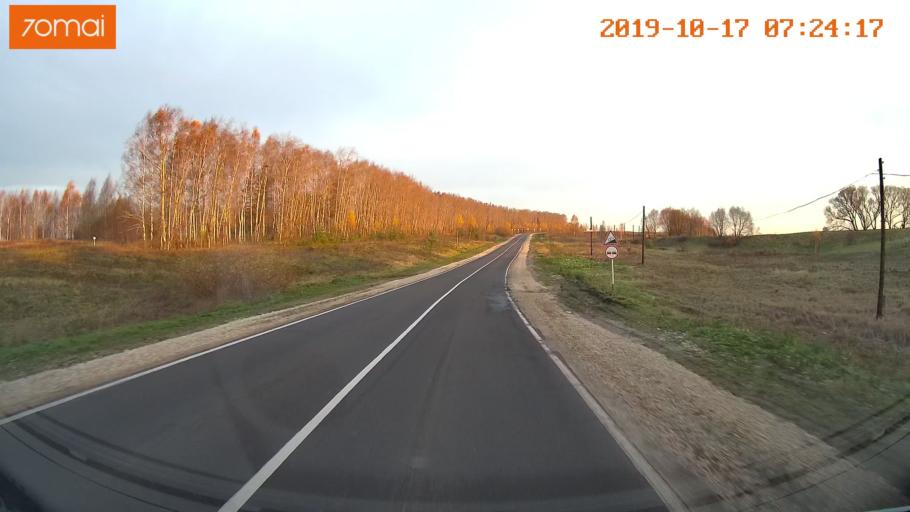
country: RU
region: Ivanovo
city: Gavrilov Posad
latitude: 56.3372
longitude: 40.1133
